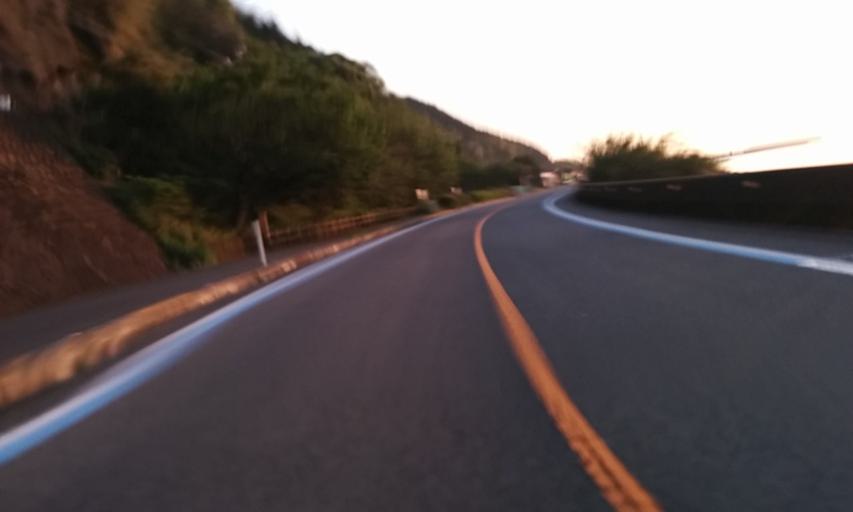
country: JP
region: Ehime
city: Iyo
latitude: 33.6925
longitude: 132.6475
